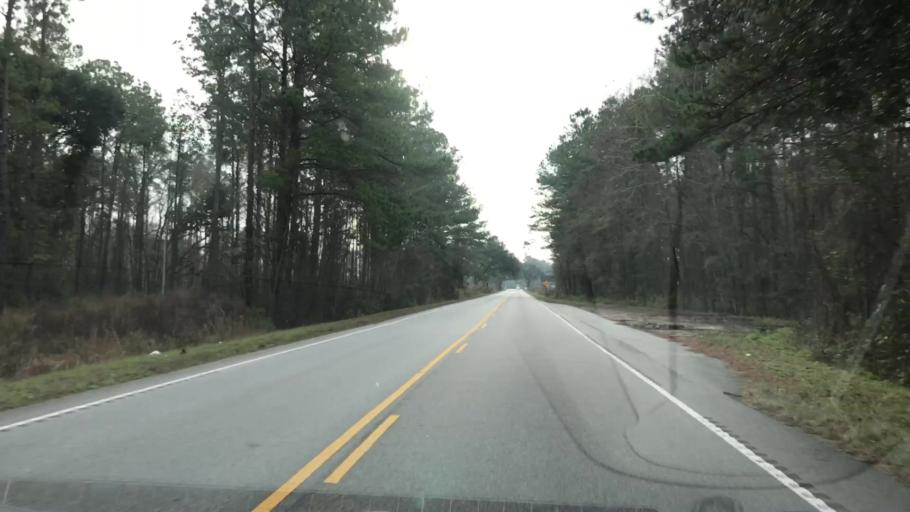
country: US
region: South Carolina
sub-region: Jasper County
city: Ridgeland
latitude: 32.5763
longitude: -80.9270
